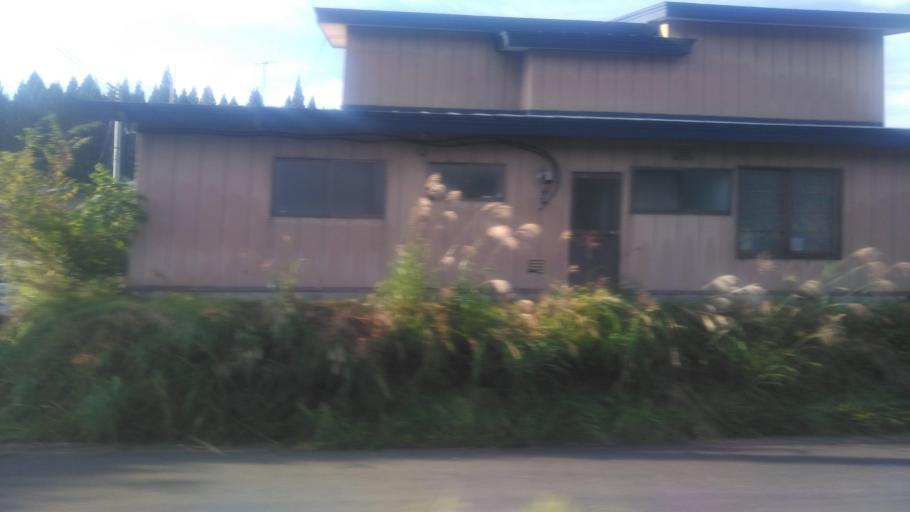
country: JP
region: Akita
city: Odate
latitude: 40.2795
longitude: 140.4622
